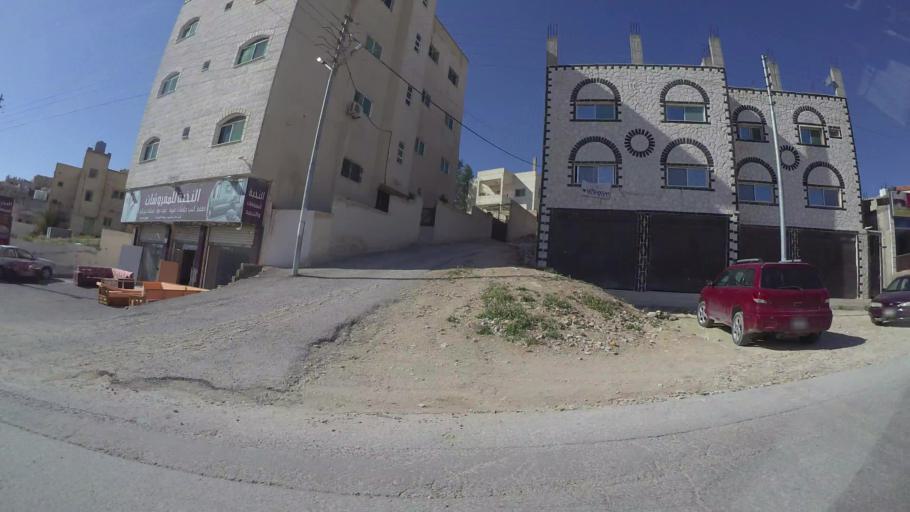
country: JO
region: Zarqa
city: Russeifa
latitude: 32.0400
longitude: 36.0527
